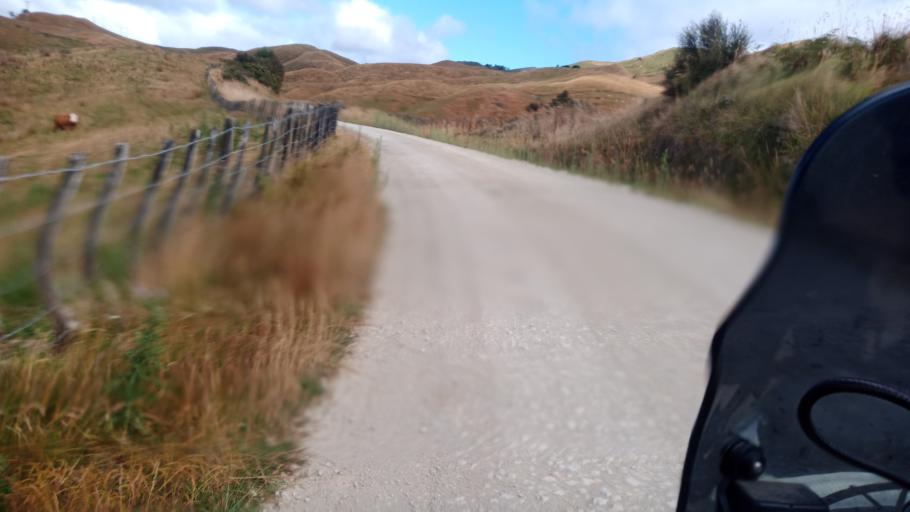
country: NZ
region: Hawke's Bay
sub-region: Wairoa District
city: Wairoa
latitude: -38.6037
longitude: 177.4708
